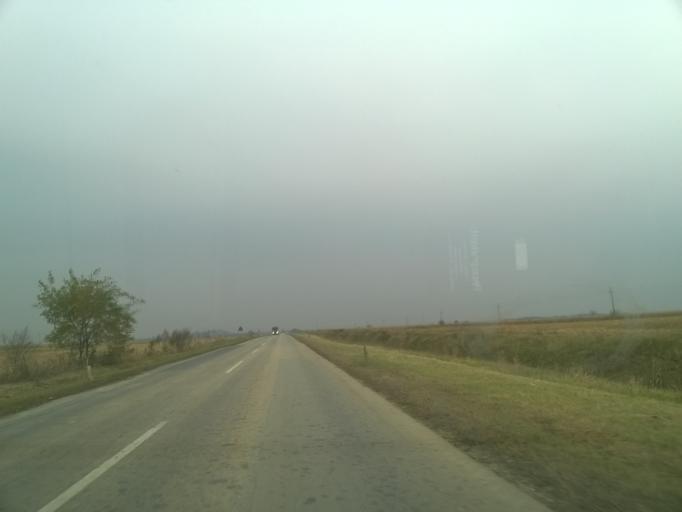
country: RS
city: Debeljaca
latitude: 45.0568
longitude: 20.6398
